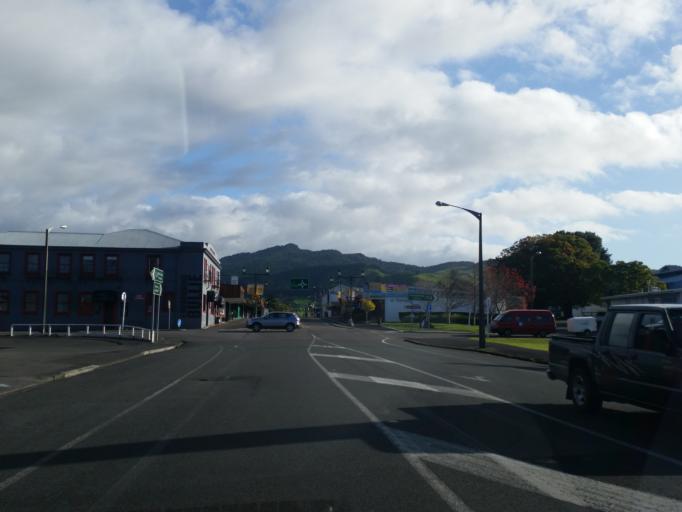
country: NZ
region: Waikato
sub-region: Hauraki District
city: Waihi
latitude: -37.3932
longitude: 175.8418
